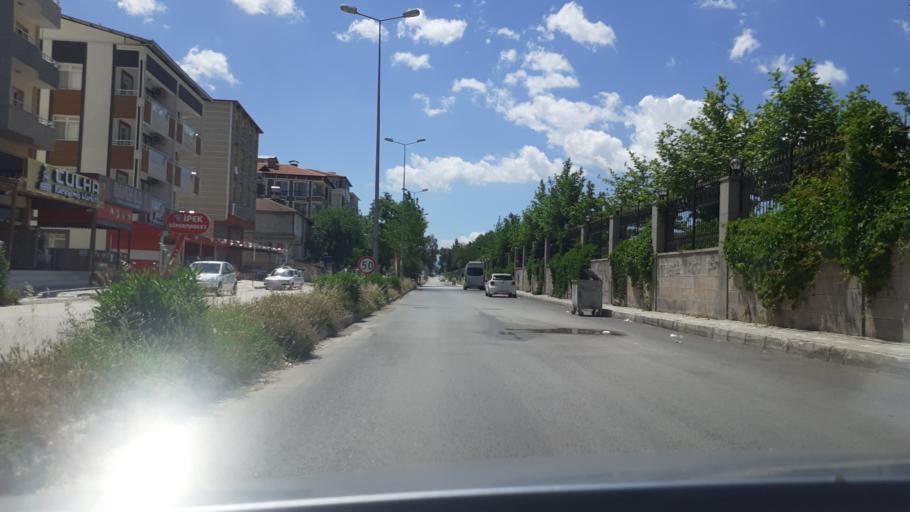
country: TR
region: Hatay
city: Anayazi
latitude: 36.3327
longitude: 36.1995
